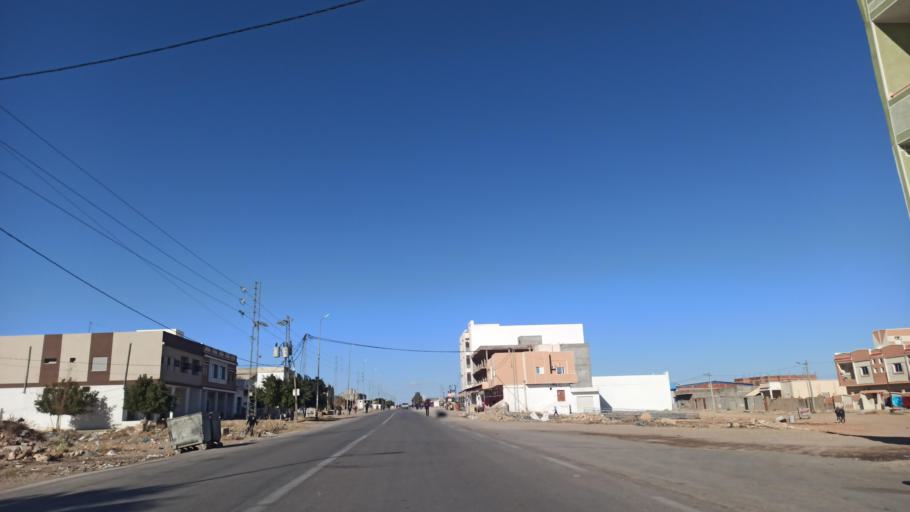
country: TN
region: Sidi Bu Zayd
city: Jilma
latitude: 35.2800
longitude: 9.4189
